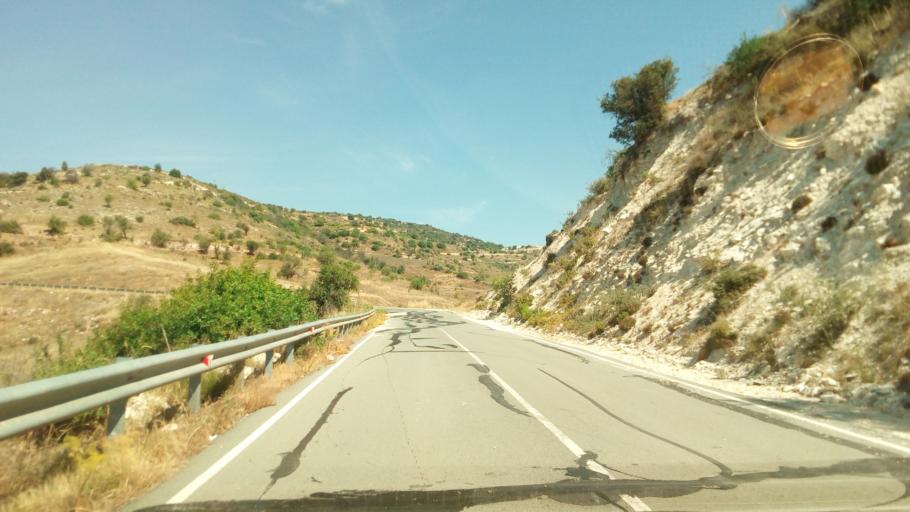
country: CY
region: Limassol
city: Pachna
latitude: 34.8014
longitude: 32.6867
